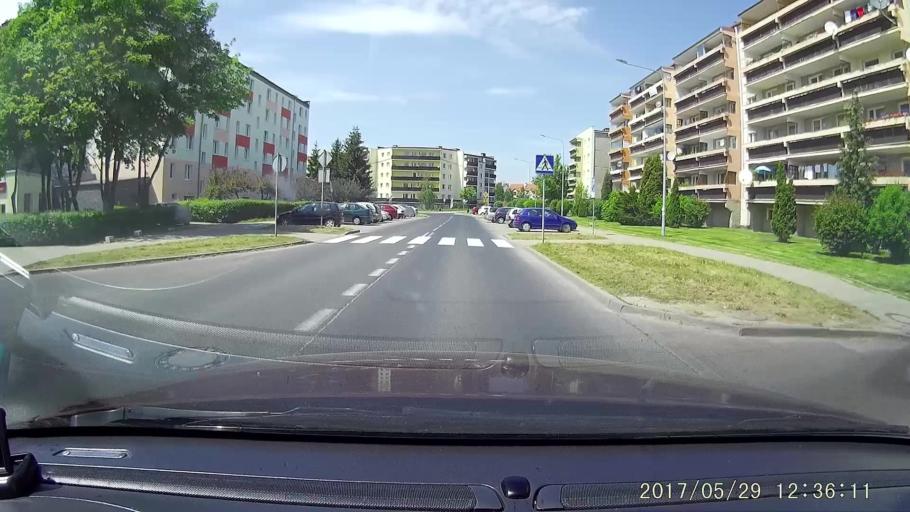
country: PL
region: Lower Silesian Voivodeship
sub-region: Powiat jeleniogorski
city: Jezow Sudecki
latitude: 50.9218
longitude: 15.7564
